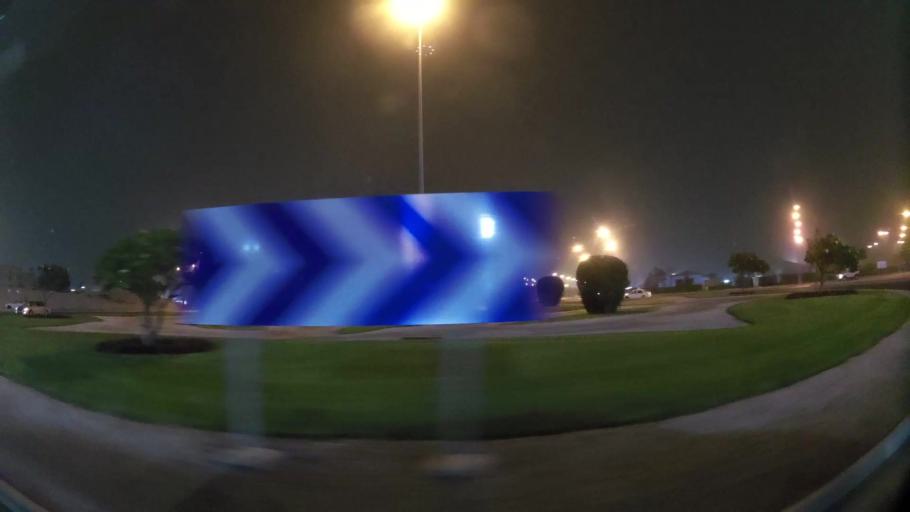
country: QA
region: Baladiyat ar Rayyan
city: Ar Rayyan
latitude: 25.2681
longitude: 51.4471
